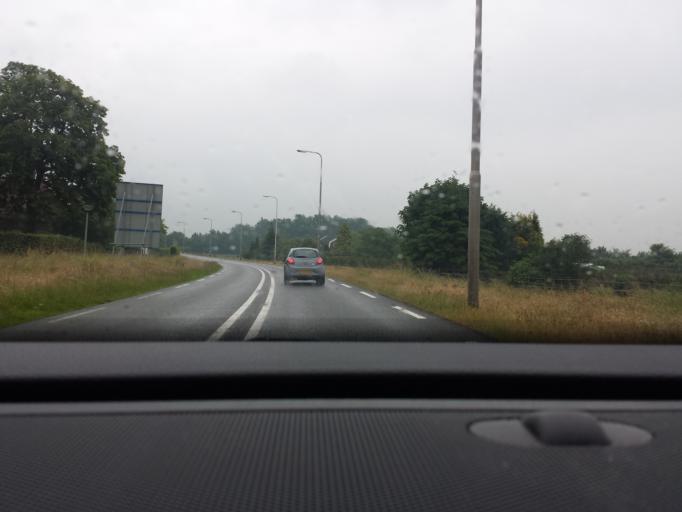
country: NL
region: Overijssel
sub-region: Gemeente Haaksbergen
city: Haaksbergen
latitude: 52.1508
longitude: 6.7462
